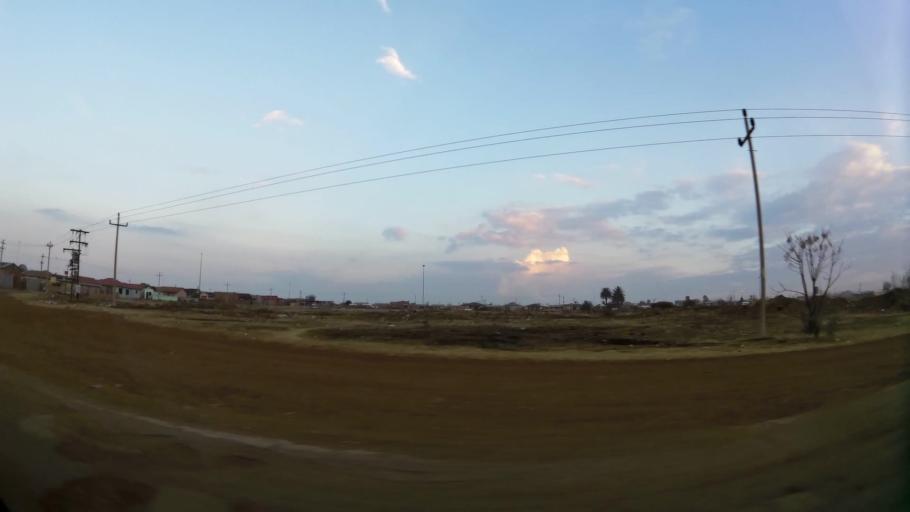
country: ZA
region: Gauteng
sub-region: City of Johannesburg Metropolitan Municipality
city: Orange Farm
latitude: -26.5459
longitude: 27.8785
